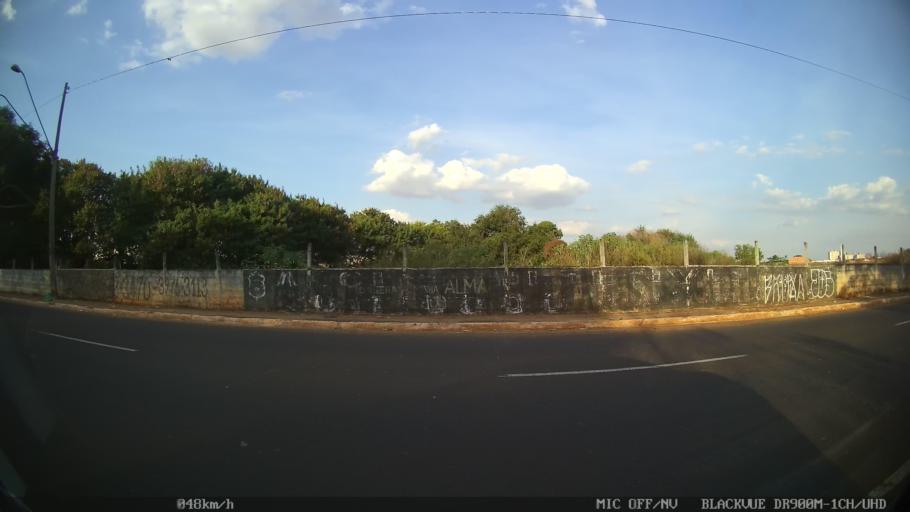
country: BR
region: Sao Paulo
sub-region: Ribeirao Preto
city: Ribeirao Preto
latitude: -21.1444
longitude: -47.8023
